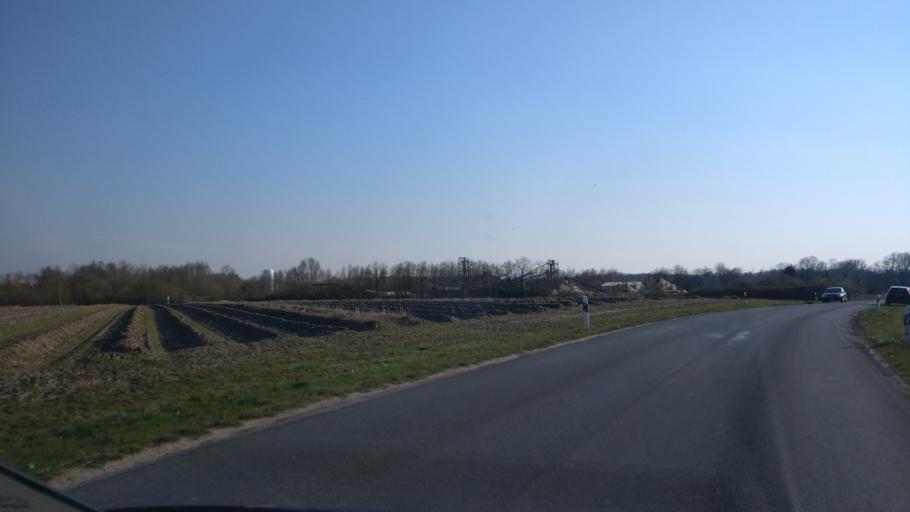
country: DE
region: North Rhine-Westphalia
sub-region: Regierungsbezirk Detmold
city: Lage
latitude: 52.0222
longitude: 8.7562
